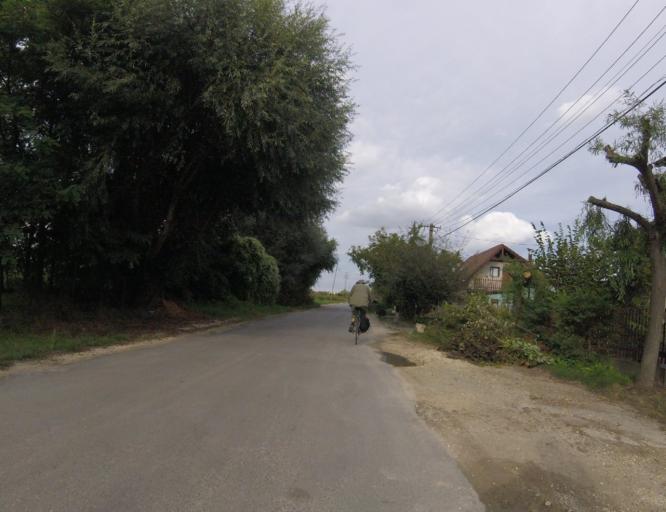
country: HU
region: Budapest
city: Budapest XXIII. keruelet
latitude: 47.3841
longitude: 19.0993
